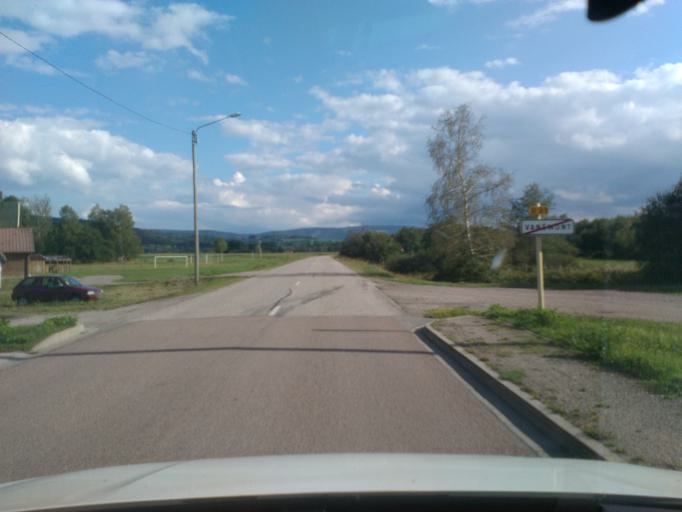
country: FR
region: Lorraine
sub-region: Departement des Vosges
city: Corcieux
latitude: 48.1972
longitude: 6.8785
